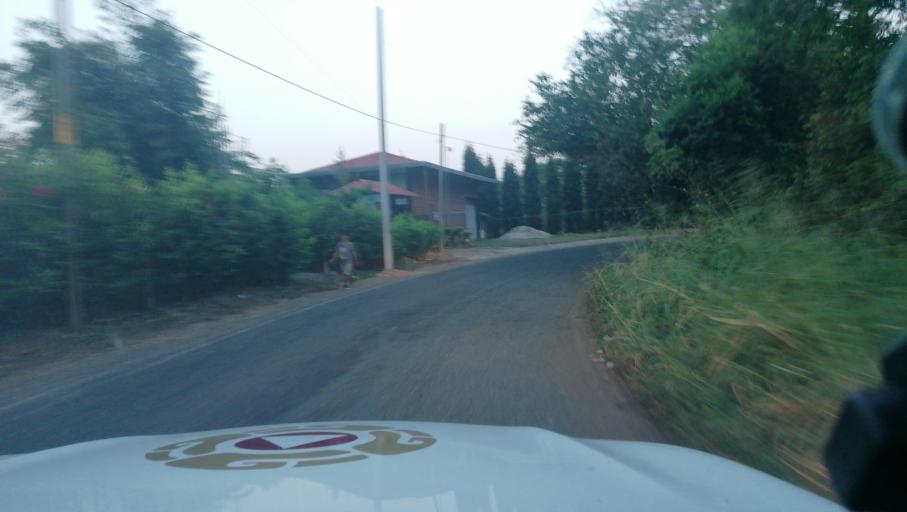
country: MX
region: Chiapas
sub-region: Cacahoatan
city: Benito Juarez
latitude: 15.0305
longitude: -92.2397
